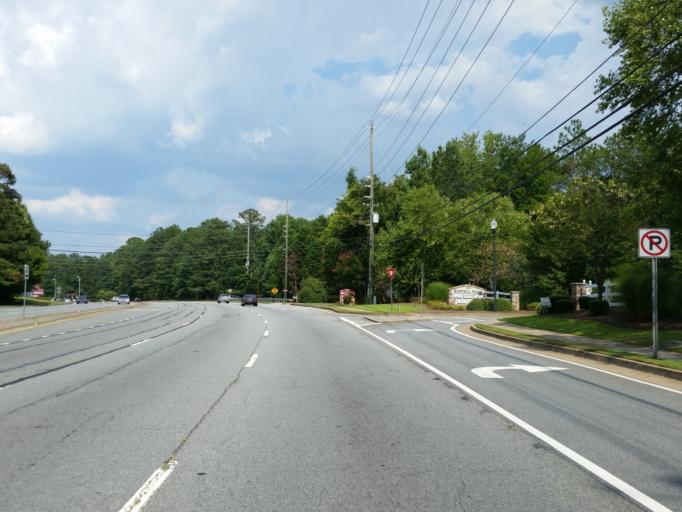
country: US
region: Georgia
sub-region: Fulton County
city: Roswell
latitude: 34.0600
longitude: -84.4154
